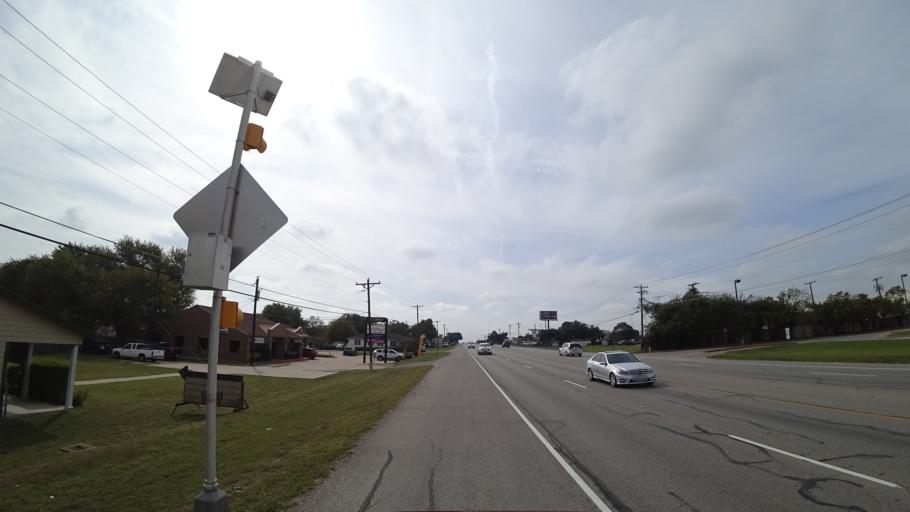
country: US
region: Texas
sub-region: Travis County
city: Wells Branch
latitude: 30.4465
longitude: -97.6629
